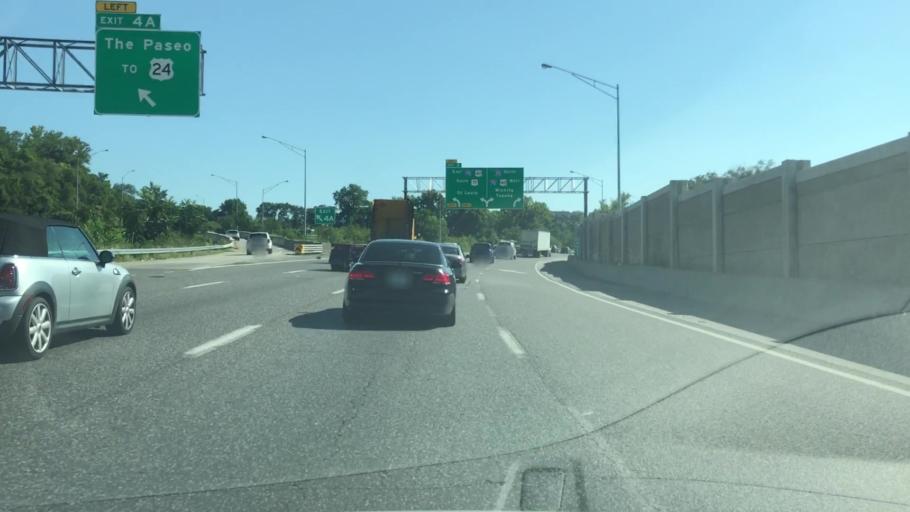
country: US
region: Missouri
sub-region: Jackson County
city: Kansas City
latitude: 39.1119
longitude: -94.5649
